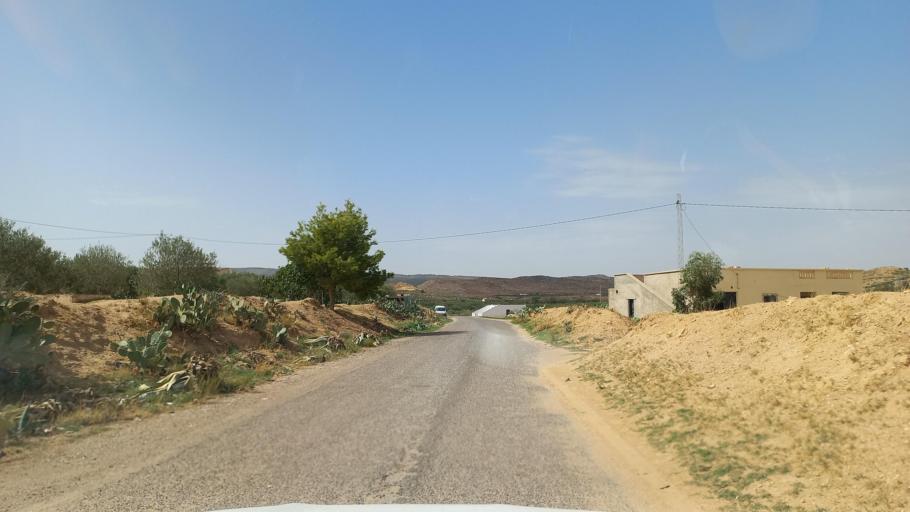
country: TN
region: Al Qasrayn
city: Kasserine
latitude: 35.2968
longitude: 8.9568
